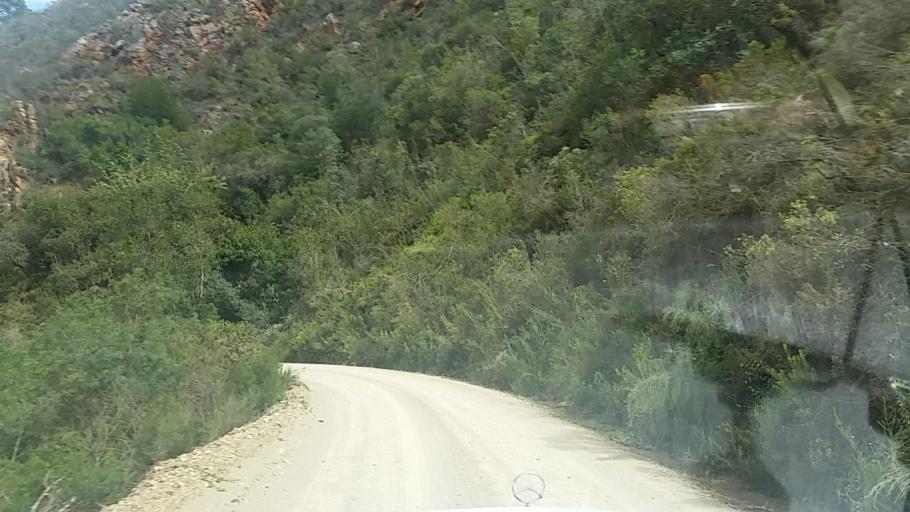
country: ZA
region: Western Cape
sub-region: Eden District Municipality
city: Knysna
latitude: -33.8083
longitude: 23.1786
